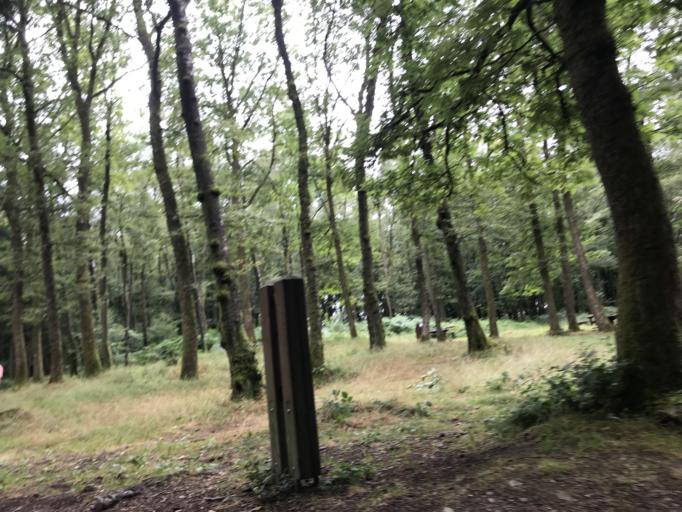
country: FR
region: Champagne-Ardenne
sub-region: Departement des Ardennes
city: Thilay
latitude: 49.8925
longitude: 4.7829
